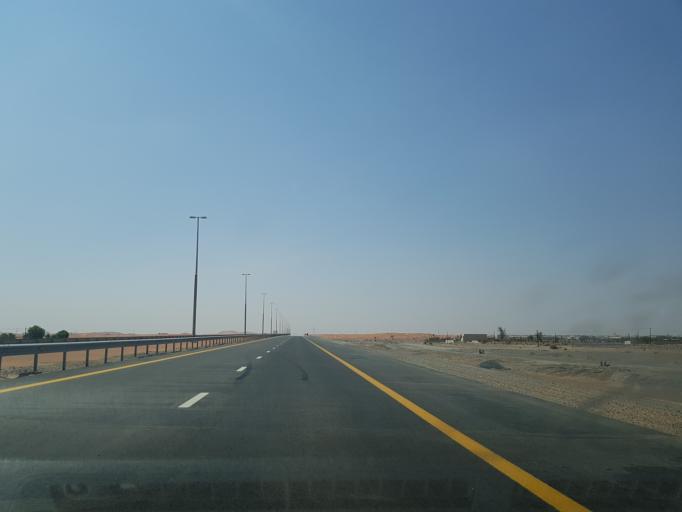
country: AE
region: Ash Shariqah
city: Adh Dhayd
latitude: 25.2379
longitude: 55.8950
